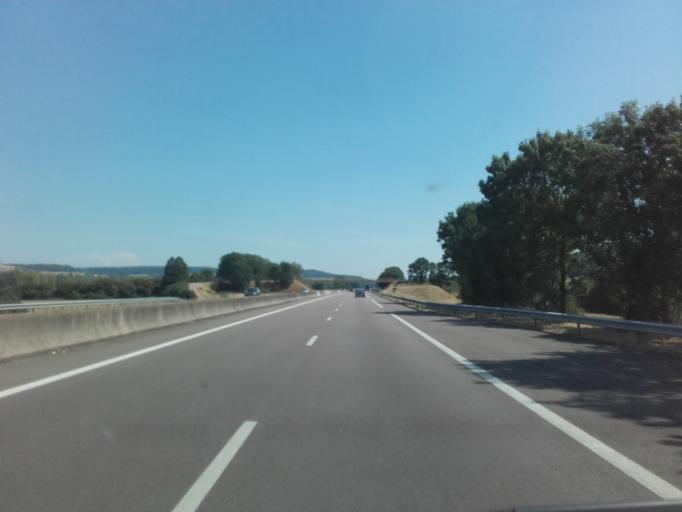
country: FR
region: Bourgogne
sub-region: Departement de la Cote-d'Or
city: Vitteaux
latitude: 47.3269
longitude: 4.4846
